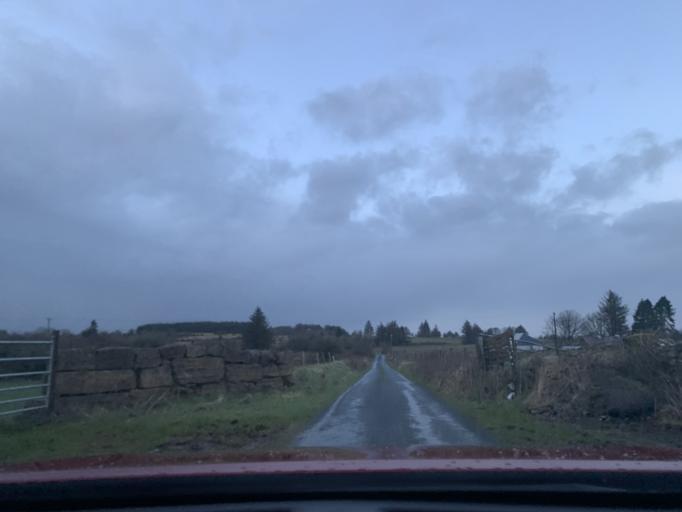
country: IE
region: Connaught
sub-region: Roscommon
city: Ballaghaderreen
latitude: 53.9707
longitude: -8.5592
